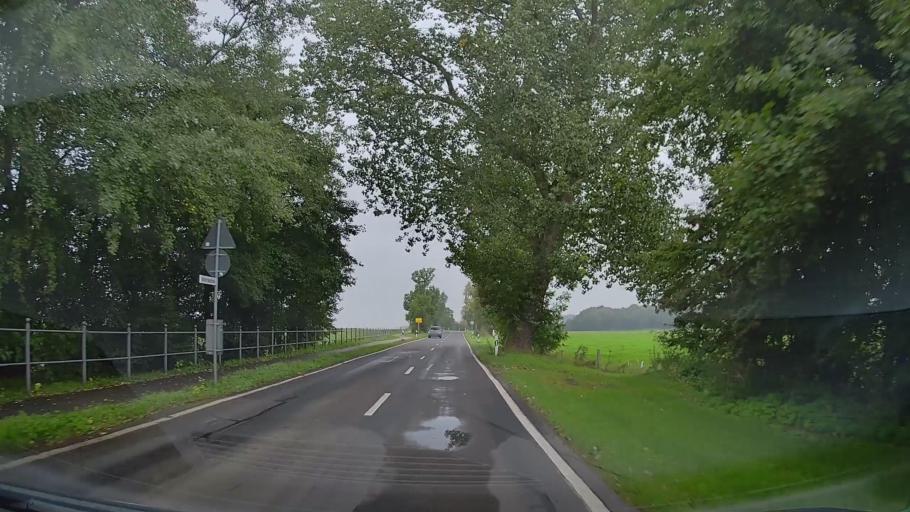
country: DE
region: Mecklenburg-Vorpommern
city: Neubukow
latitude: 54.0763
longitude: 11.6332
